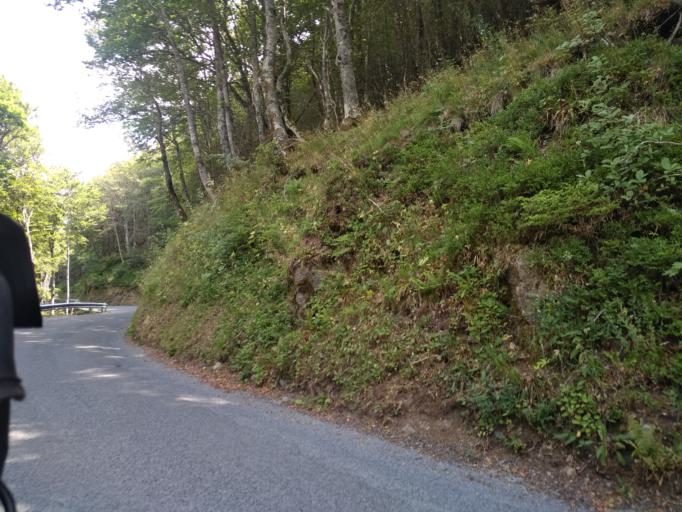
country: FR
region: Auvergne
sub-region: Departement du Cantal
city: Riom-es-Montagnes
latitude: 45.1280
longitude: 2.6978
